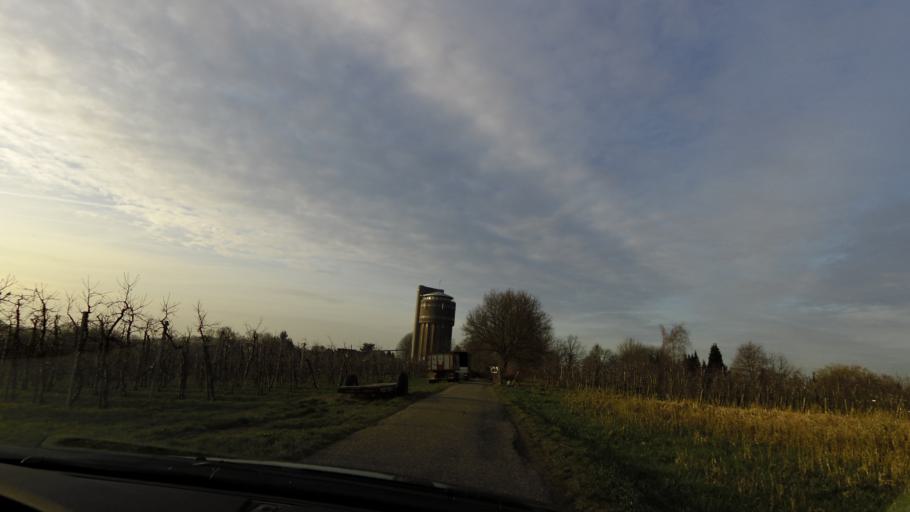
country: NL
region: Limburg
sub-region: Valkenburg aan de Geul
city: Broekhem
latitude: 50.8997
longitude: 5.8255
